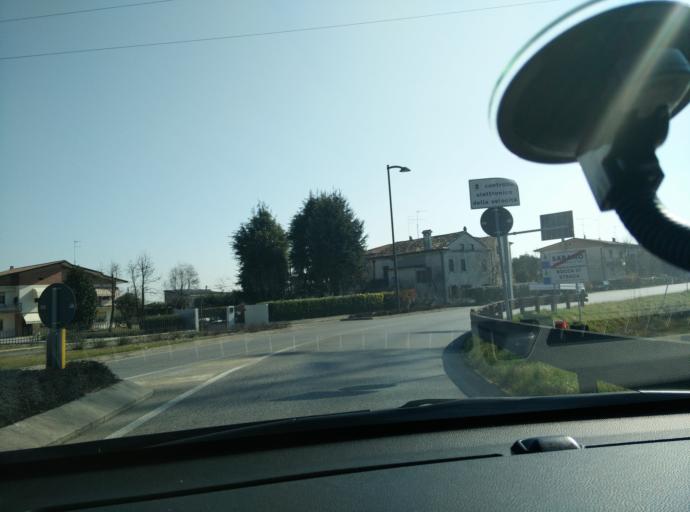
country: IT
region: Veneto
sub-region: Provincia di Treviso
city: Santa Lucia di Piave
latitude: 45.8558
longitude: 12.3062
